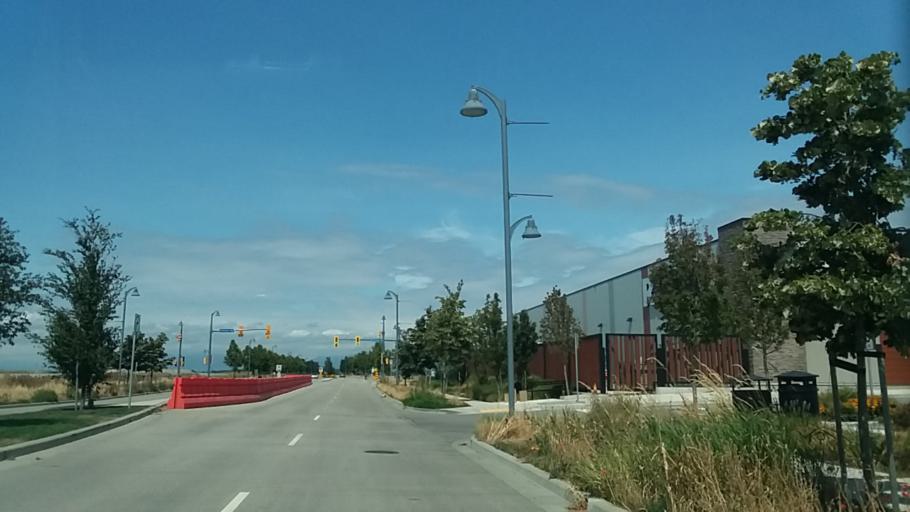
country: CA
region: British Columbia
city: Ladner
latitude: 49.0420
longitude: -123.0902
